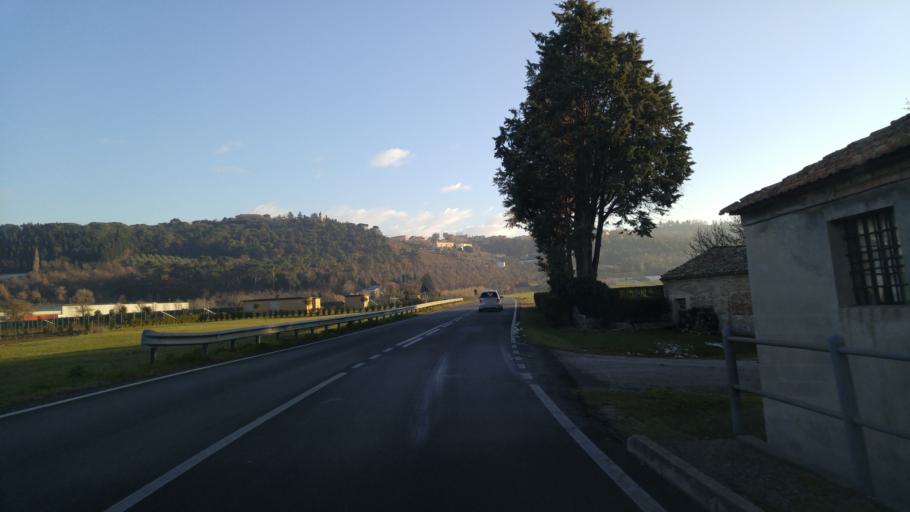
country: IT
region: The Marches
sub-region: Provincia di Ancona
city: Monterado
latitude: 43.7043
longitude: 13.0836
